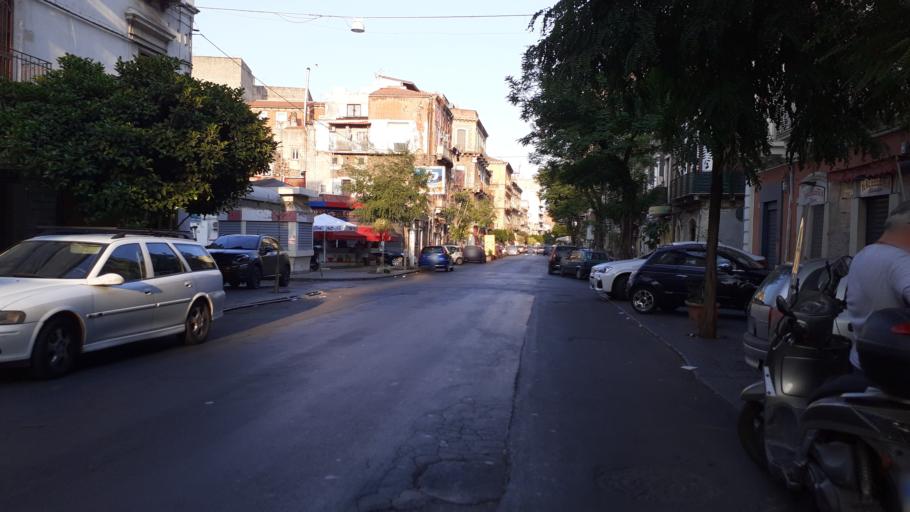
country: IT
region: Sicily
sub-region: Catania
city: Catania
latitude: 37.4990
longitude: 15.0783
